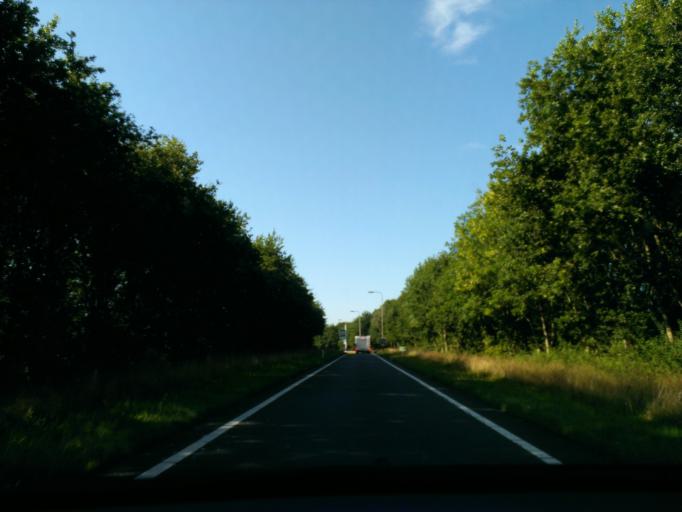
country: NL
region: Drenthe
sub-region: Gemeente Coevorden
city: Coevorden
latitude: 52.6782
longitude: 6.7299
